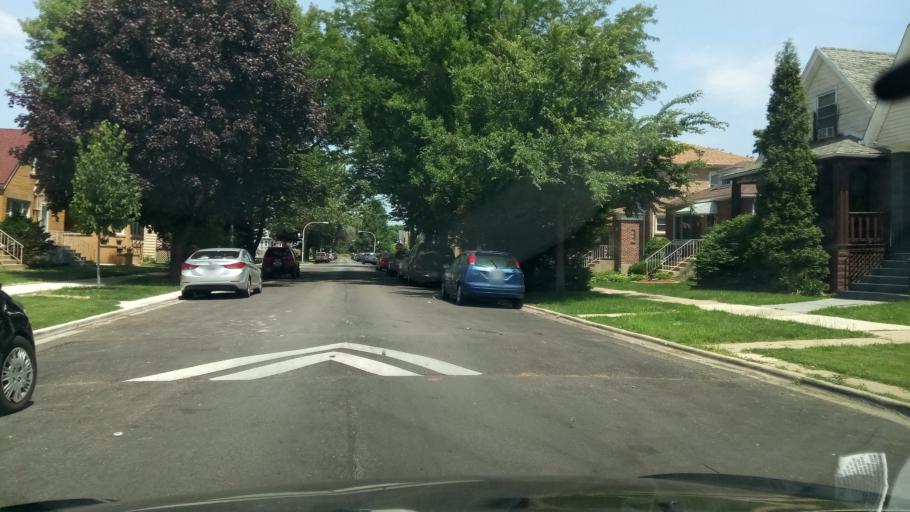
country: US
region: Illinois
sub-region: Cook County
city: Hometown
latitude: 41.7814
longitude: -87.7314
